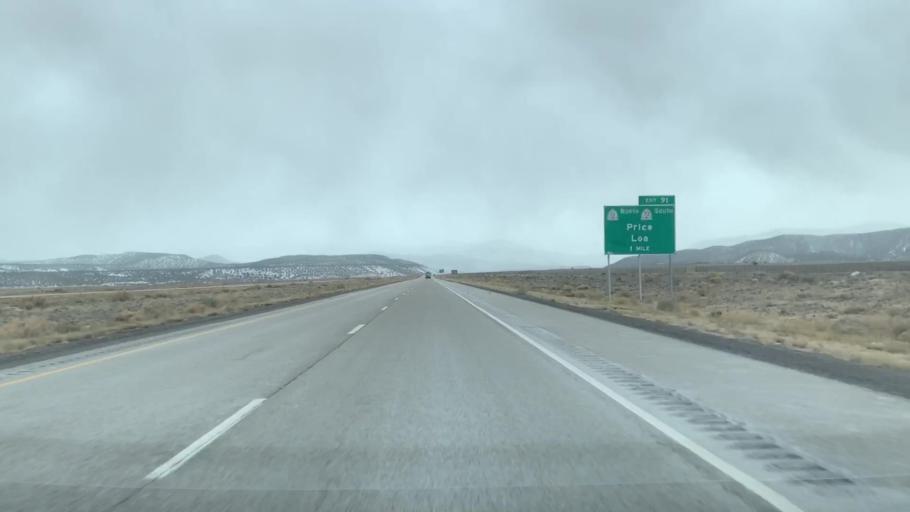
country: US
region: Utah
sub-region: Emery County
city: Ferron
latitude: 38.7756
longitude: -111.3253
